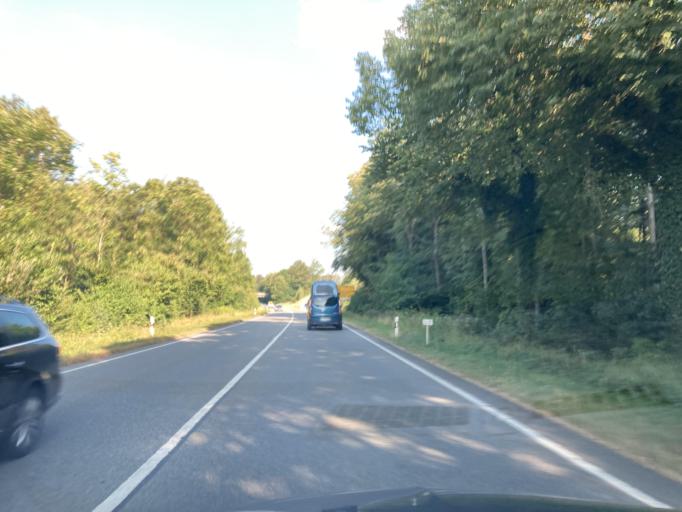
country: DE
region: Bavaria
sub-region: Upper Bavaria
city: Wasserburg am Inn
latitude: 48.0667
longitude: 12.2406
